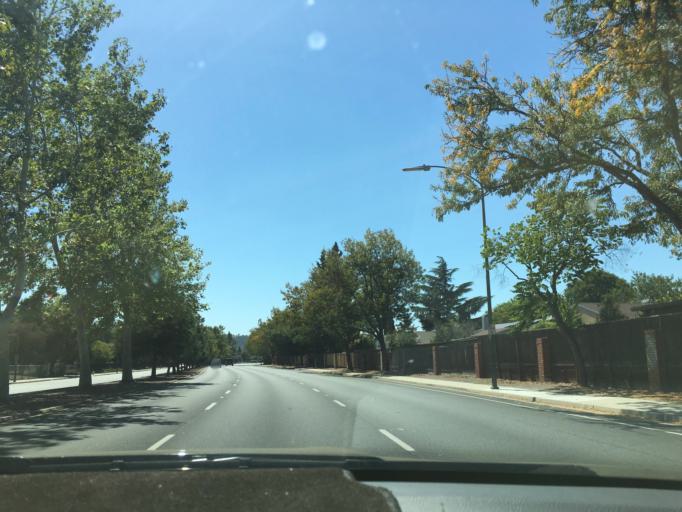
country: US
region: California
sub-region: Santa Clara County
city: Seven Trees
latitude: 37.2375
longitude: -121.8262
